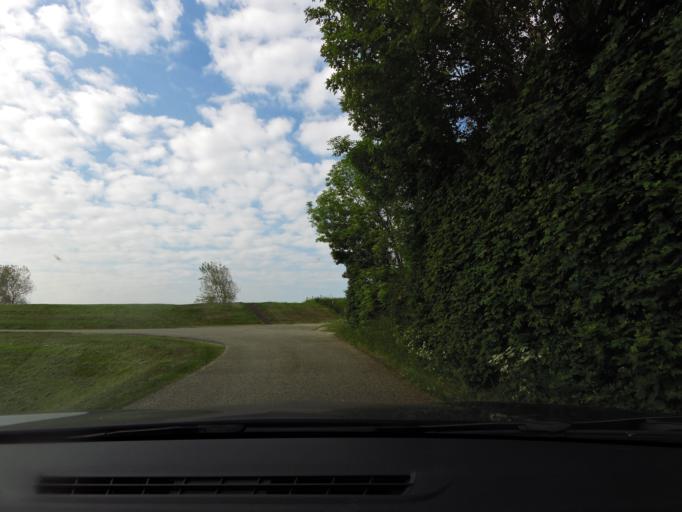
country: NL
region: Zeeland
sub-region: Schouwen-Duiveland
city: Renesse
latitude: 51.6988
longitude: 3.8107
